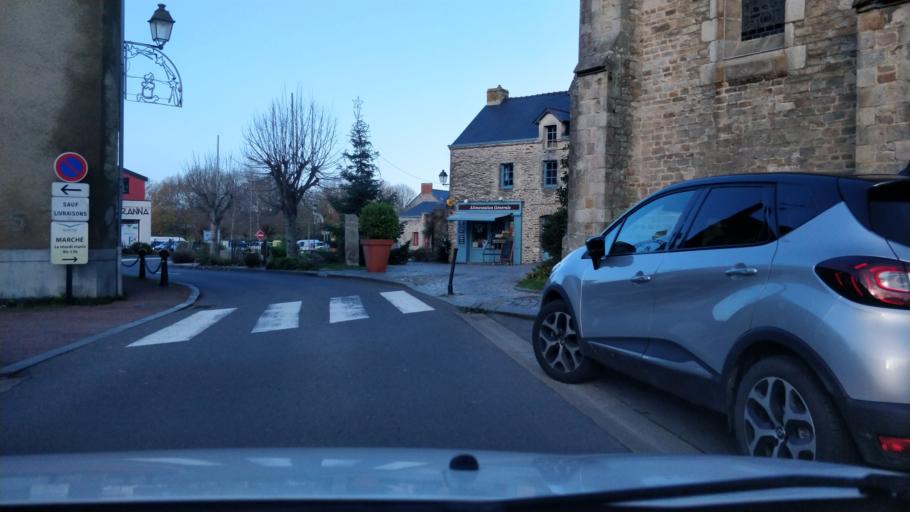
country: FR
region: Pays de la Loire
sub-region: Departement de la Loire-Atlantique
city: Asserac
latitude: 47.4292
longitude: -2.3905
